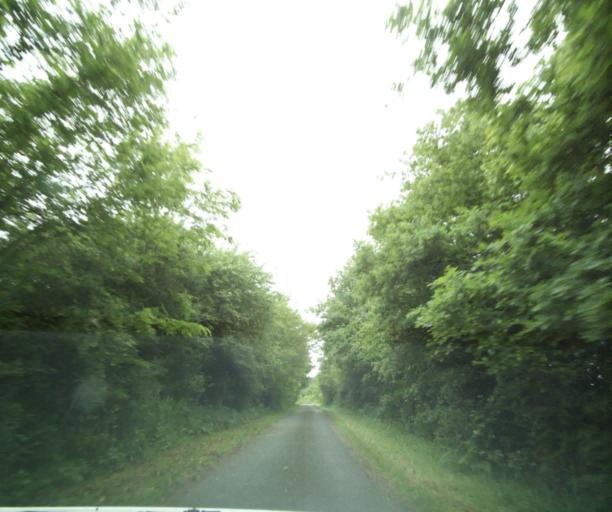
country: FR
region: Bourgogne
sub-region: Departement de Saone-et-Loire
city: Palinges
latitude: 46.5743
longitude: 4.2070
